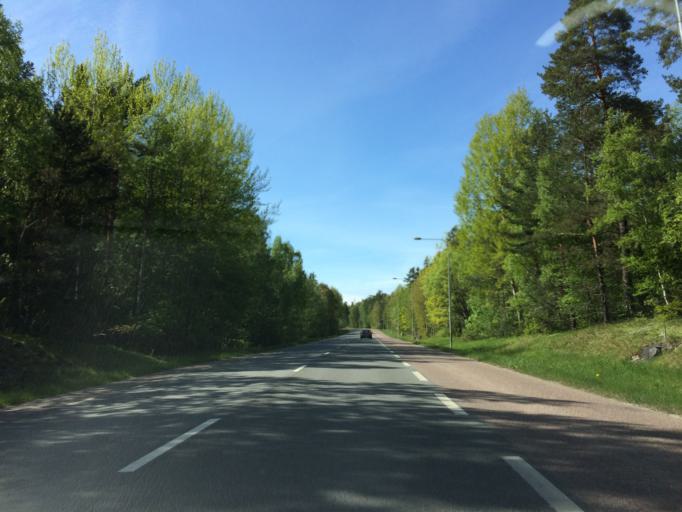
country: SE
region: Stockholm
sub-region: Sollentuna Kommun
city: Sollentuna
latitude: 59.4387
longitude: 17.9867
